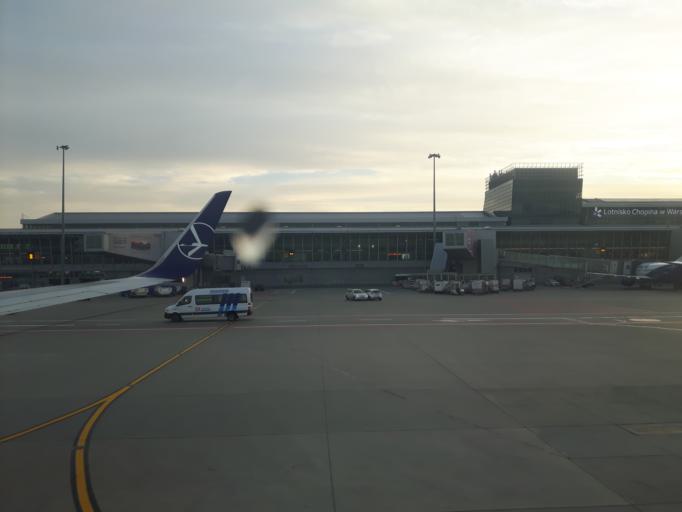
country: PL
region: Masovian Voivodeship
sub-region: Warszawa
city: Wlochy
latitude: 52.1710
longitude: 20.9690
